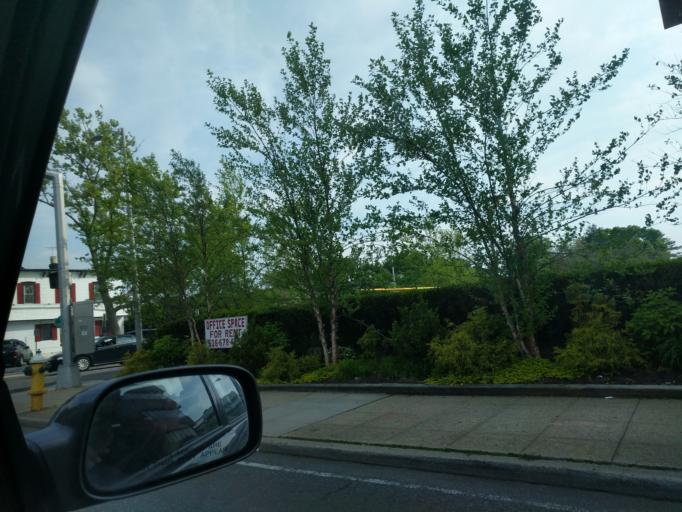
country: US
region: New York
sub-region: Nassau County
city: Rockville Centre
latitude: 40.6558
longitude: -73.6483
